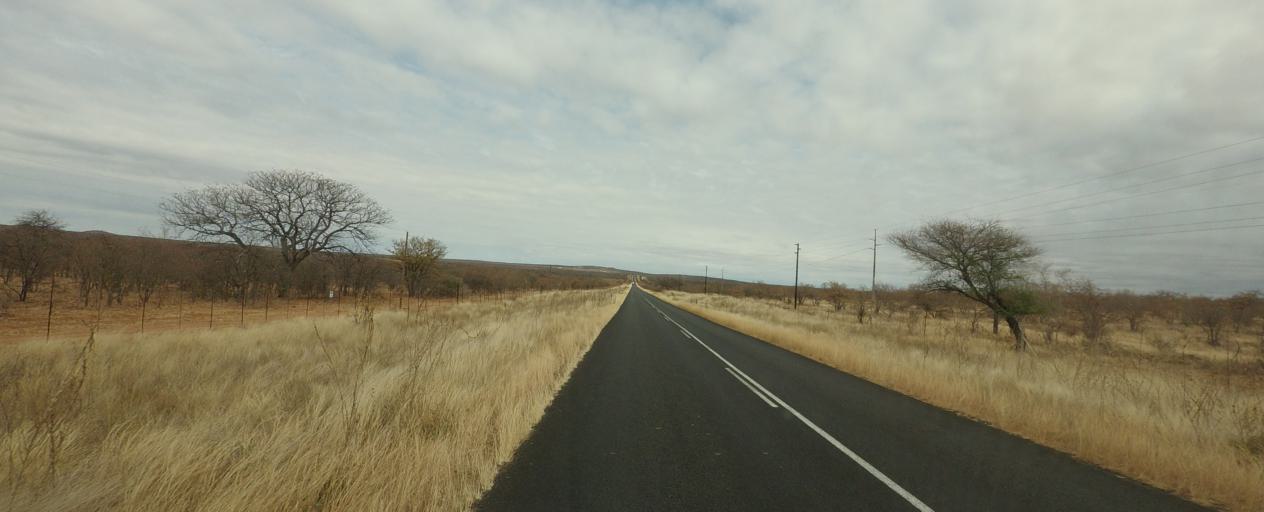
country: ZW
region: Matabeleland South
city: Beitbridge
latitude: -22.4306
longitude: 29.4469
